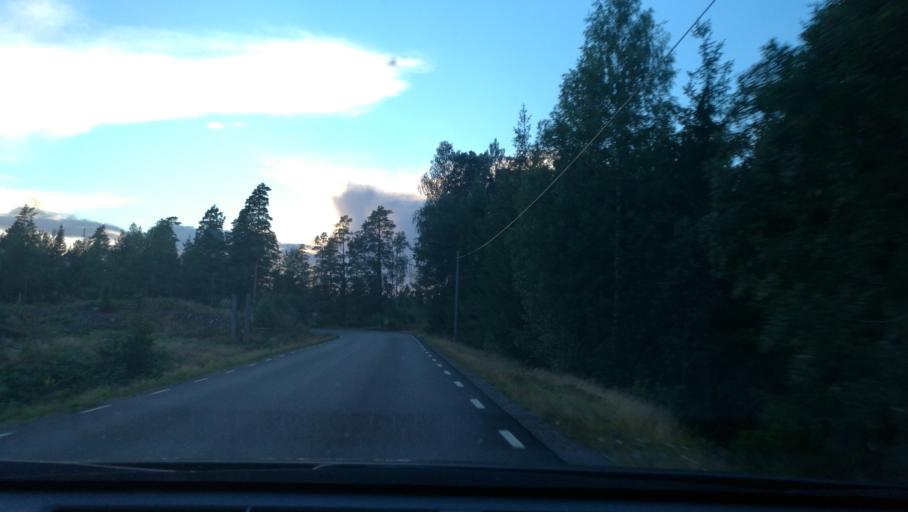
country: SE
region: OEstergoetland
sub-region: Norrkopings Kommun
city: Jursla
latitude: 58.8012
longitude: 16.1438
